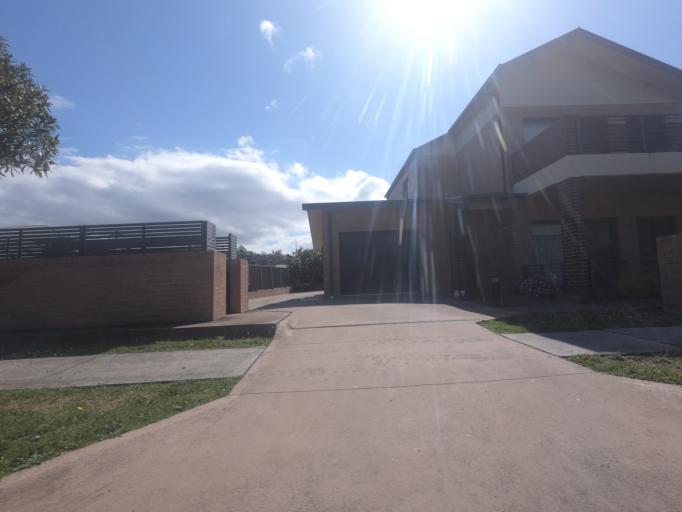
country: AU
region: New South Wales
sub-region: Wollongong
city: Cordeaux Heights
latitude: -34.4582
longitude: 150.8355
